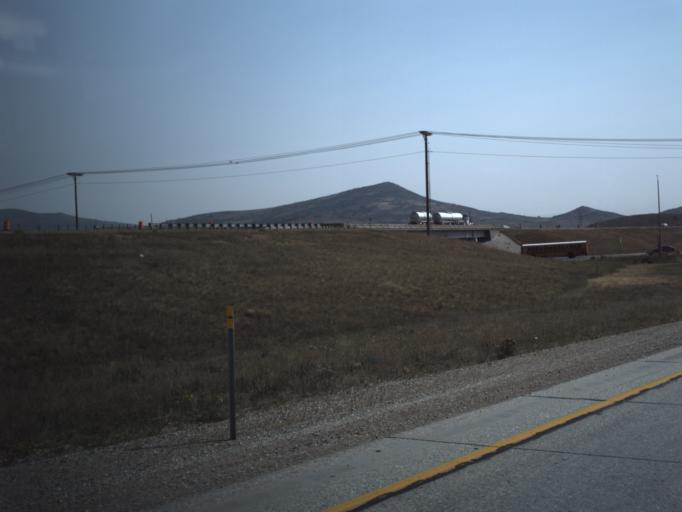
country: US
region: Utah
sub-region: Summit County
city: Park City
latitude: 40.6844
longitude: -111.4638
